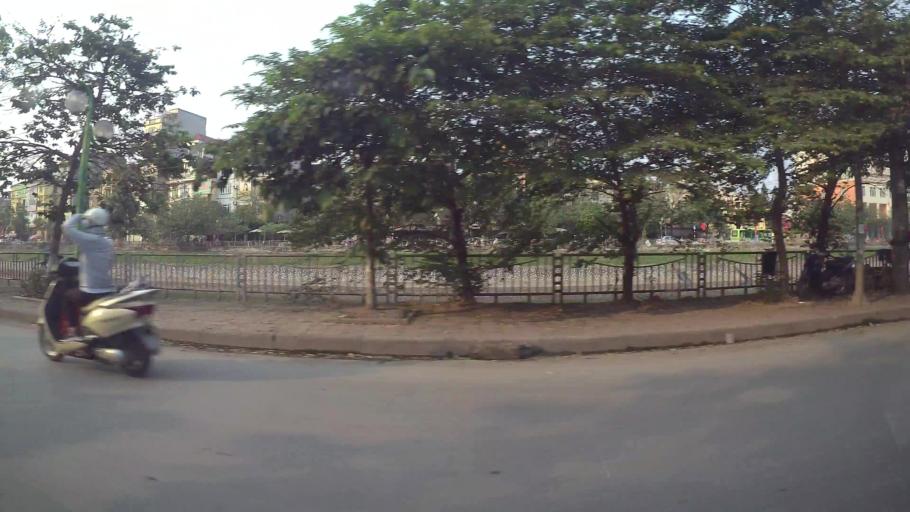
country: VN
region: Ha Noi
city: Thanh Xuan
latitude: 20.9795
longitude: 105.8202
